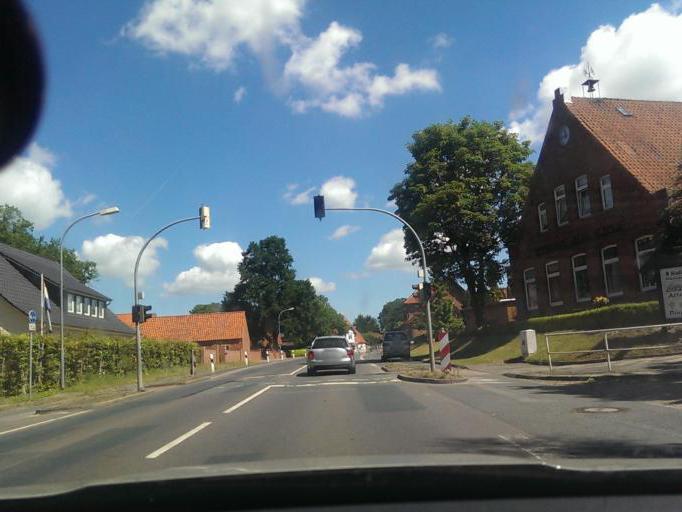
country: DE
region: Lower Saxony
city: Verden
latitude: 52.9737
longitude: 9.2539
